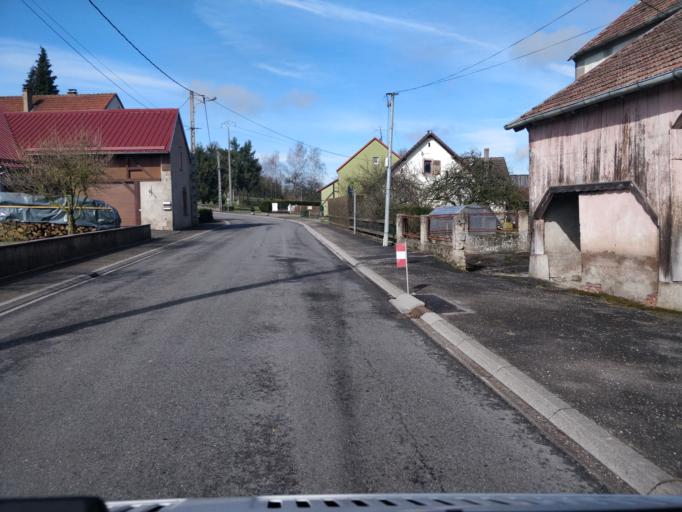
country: FR
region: Alsace
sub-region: Departement du Bas-Rhin
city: Drulingen
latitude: 48.8629
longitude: 7.2284
